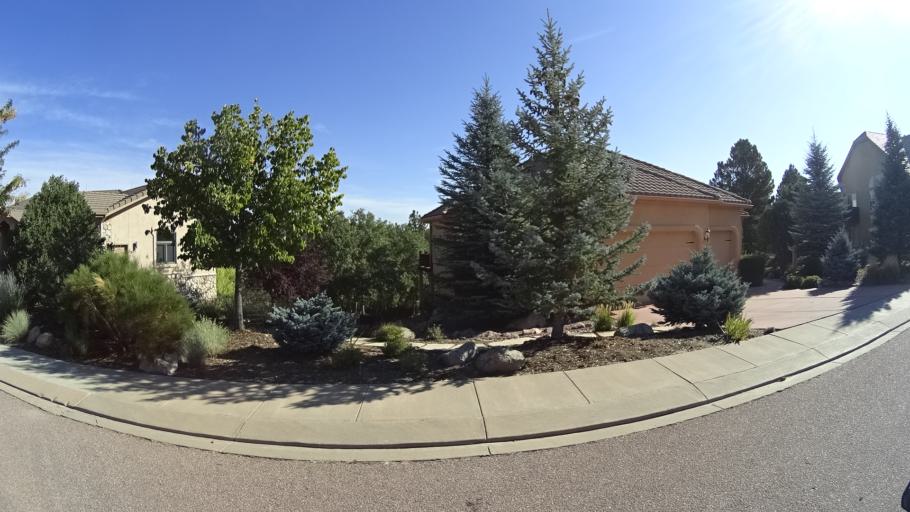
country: US
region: Colorado
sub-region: El Paso County
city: Colorado Springs
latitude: 38.9138
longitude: -104.7989
